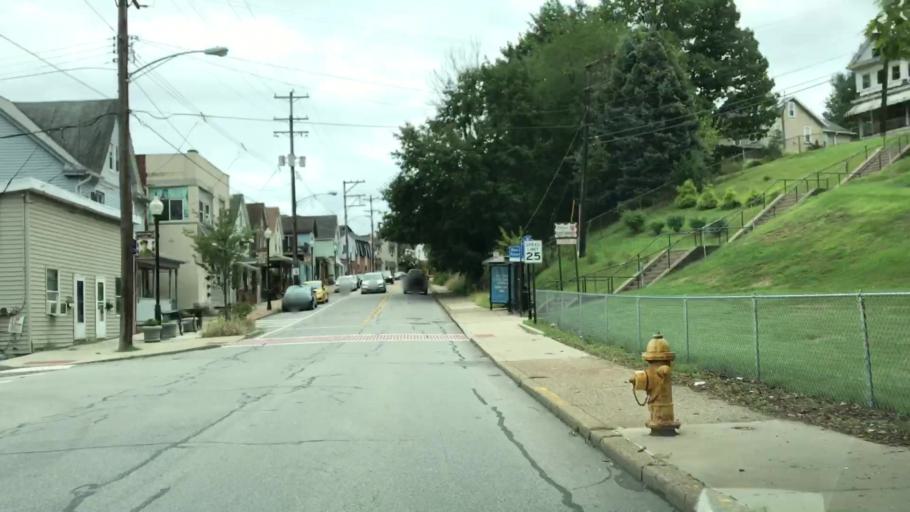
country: US
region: Pennsylvania
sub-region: Allegheny County
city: Carnegie
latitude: 40.4019
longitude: -80.0885
